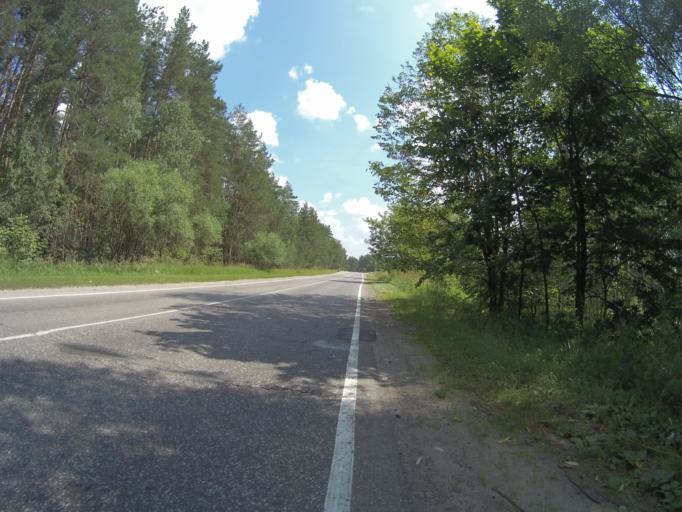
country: RU
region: Vladimir
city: Gus'-Khrustal'nyy
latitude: 55.6365
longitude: 40.7557
